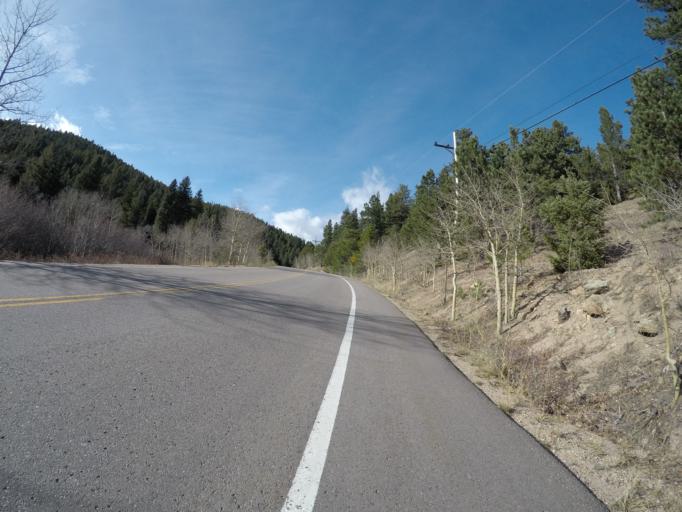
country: US
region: Colorado
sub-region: Boulder County
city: Nederland
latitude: 40.0662
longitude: -105.5028
